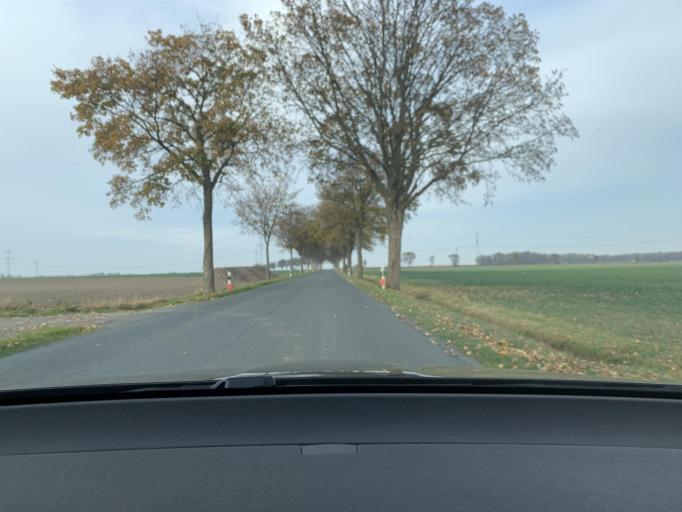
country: DE
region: Lower Saxony
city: Meine
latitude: 52.3636
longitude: 10.5529
